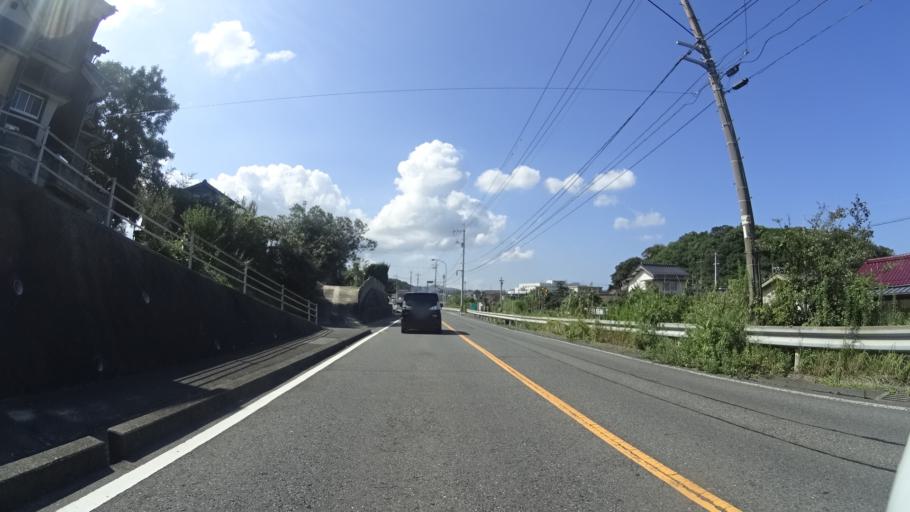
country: JP
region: Yamaguchi
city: Shimonoseki
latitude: 34.1726
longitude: 130.9297
